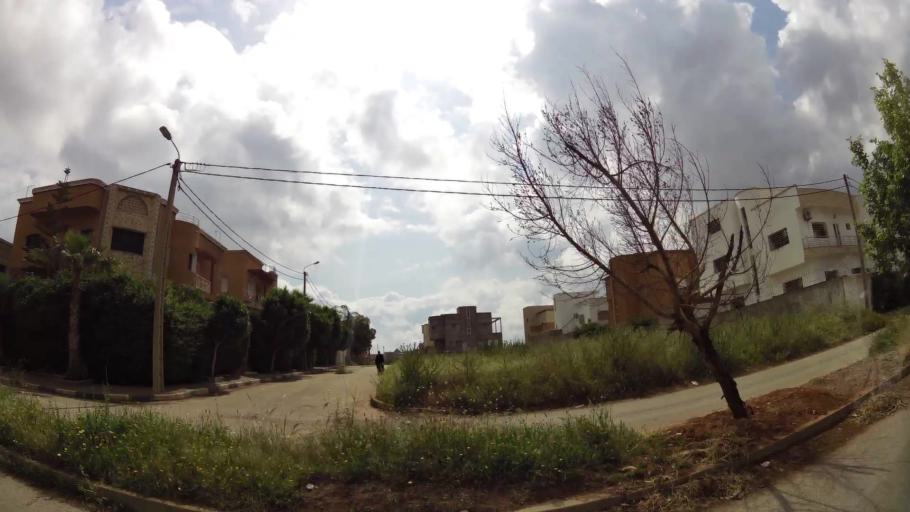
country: MA
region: Rabat-Sale-Zemmour-Zaer
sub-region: Khemisset
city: Tiflet
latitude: 33.8958
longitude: -6.3374
